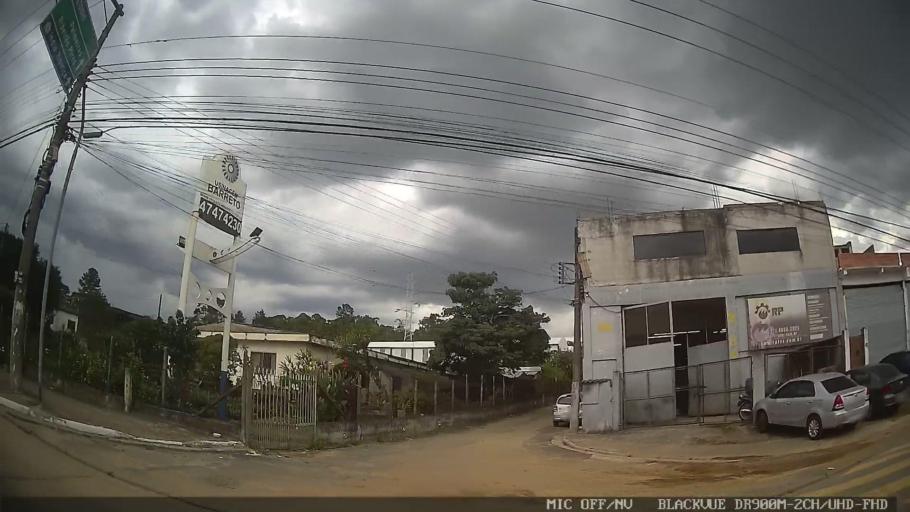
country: BR
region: Sao Paulo
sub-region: Suzano
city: Suzano
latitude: -23.5588
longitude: -46.3003
